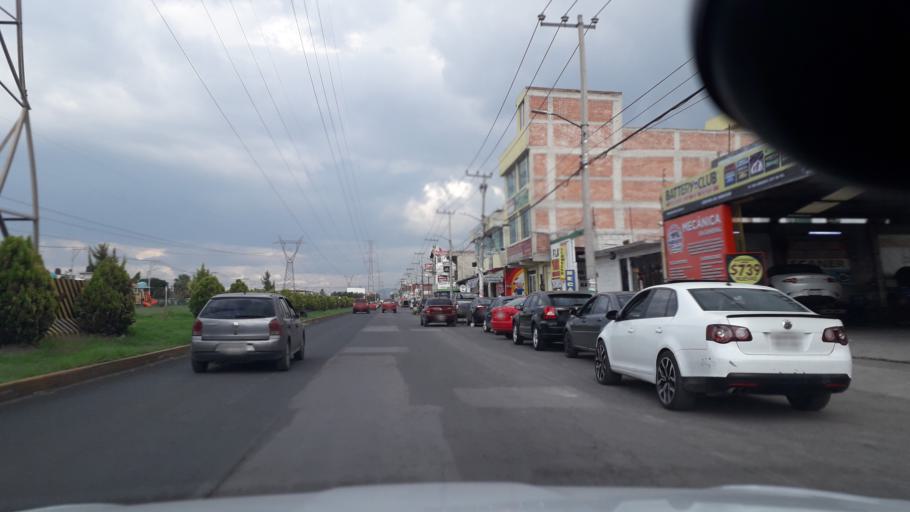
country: MX
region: Mexico
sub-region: Tultitlan
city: Fuentes del Valle
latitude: 19.6407
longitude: -99.1304
